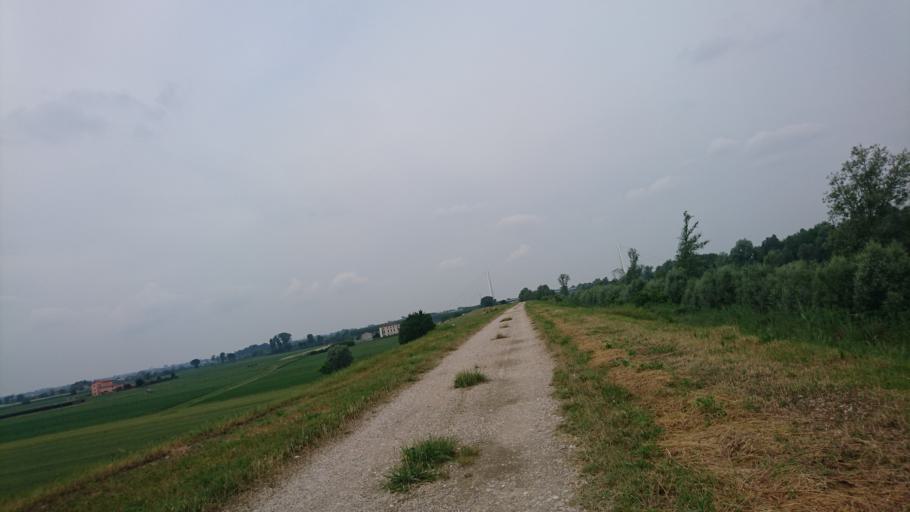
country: IT
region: Veneto
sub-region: Provincia di Padova
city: Piacenza d'Adige
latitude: 45.1198
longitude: 11.5468
